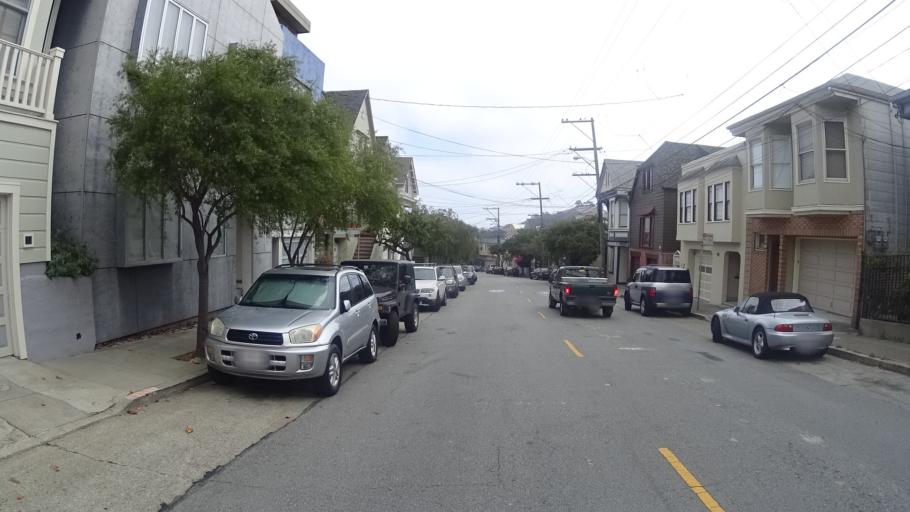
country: US
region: California
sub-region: San Francisco County
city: San Francisco
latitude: 37.7377
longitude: -122.4269
